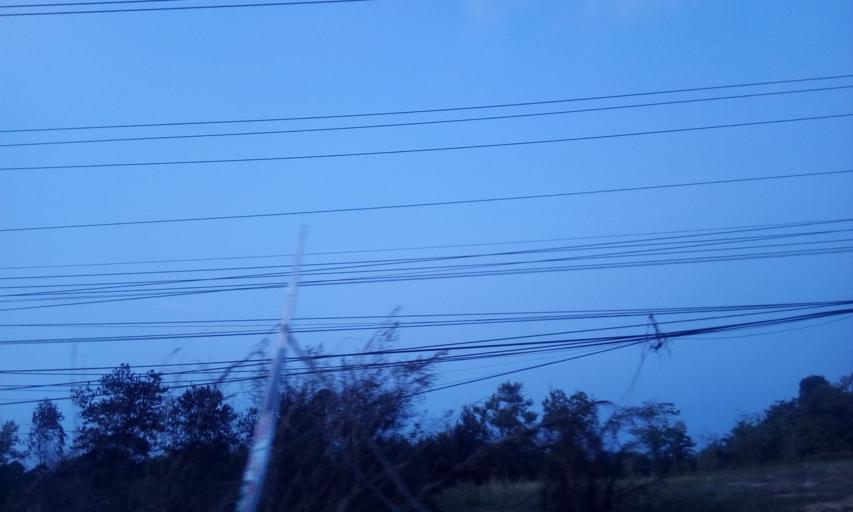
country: TH
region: Trat
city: Khao Saming
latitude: 12.3966
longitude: 102.3549
